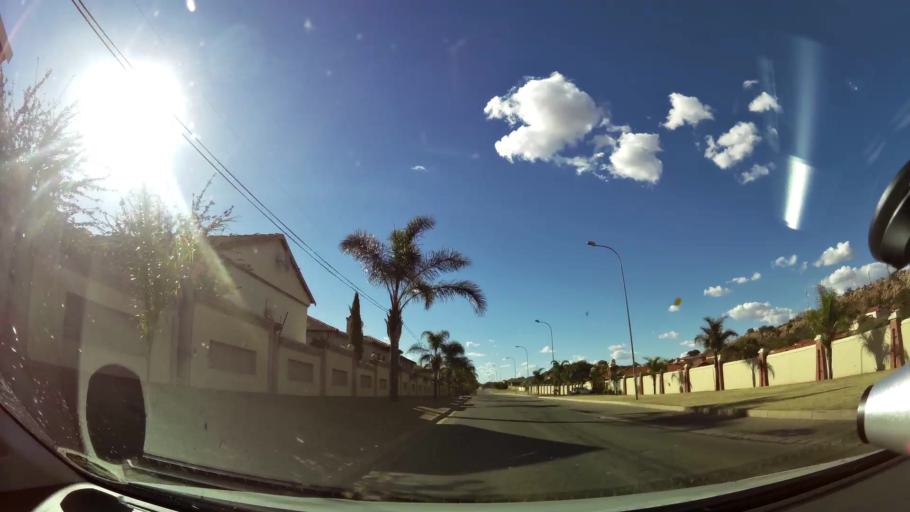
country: ZA
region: North-West
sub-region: Dr Kenneth Kaunda District Municipality
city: Klerksdorp
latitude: -26.8200
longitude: 26.6791
